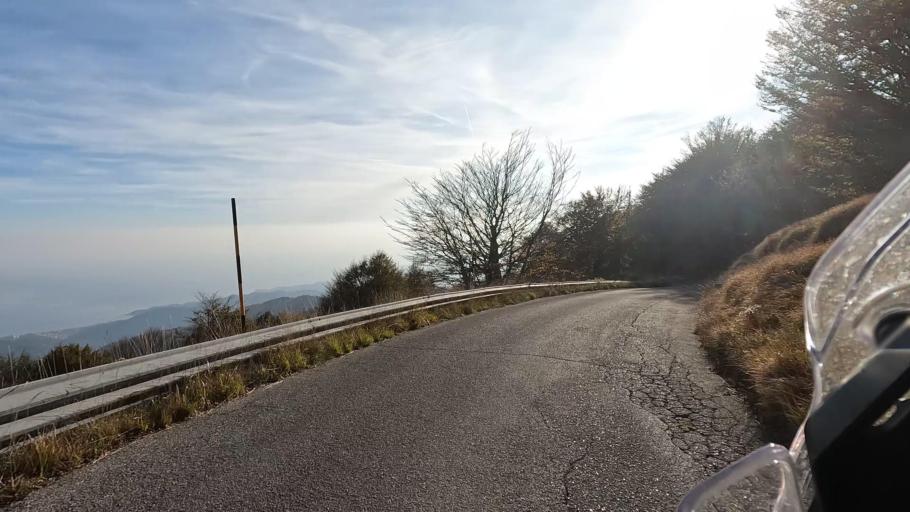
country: IT
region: Liguria
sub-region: Provincia di Savona
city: Urbe
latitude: 44.4309
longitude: 8.5570
